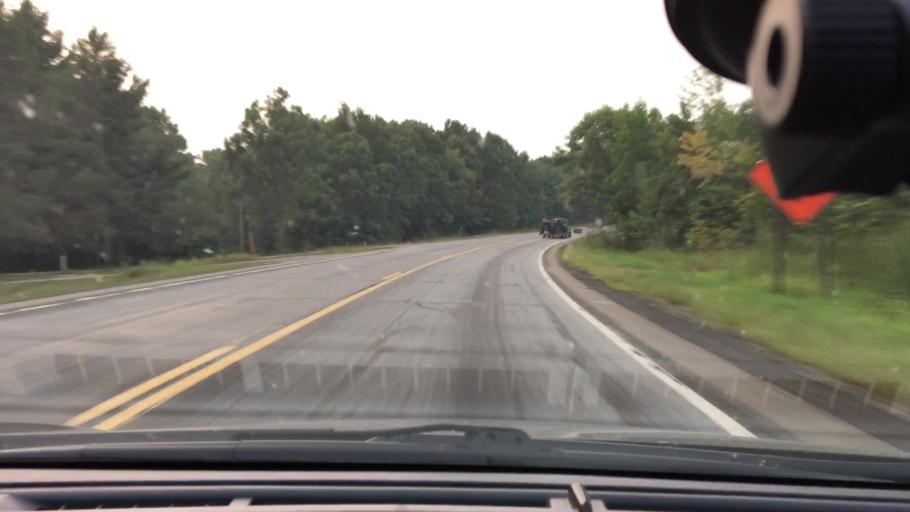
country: US
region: Minnesota
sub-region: Crow Wing County
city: Cross Lake
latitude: 46.7235
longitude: -93.9582
